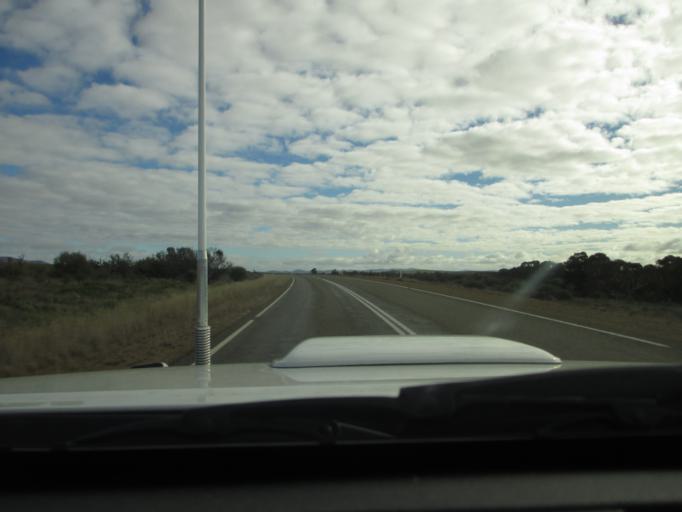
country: AU
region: South Australia
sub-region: Flinders Ranges
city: Quorn
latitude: -32.4146
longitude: 138.5221
